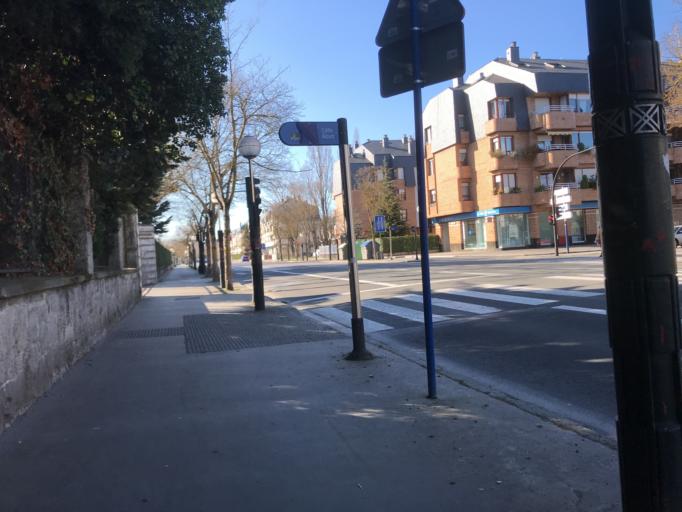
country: ES
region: Basque Country
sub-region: Provincia de Alava
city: Gasteiz / Vitoria
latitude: 42.8373
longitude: -2.6780
